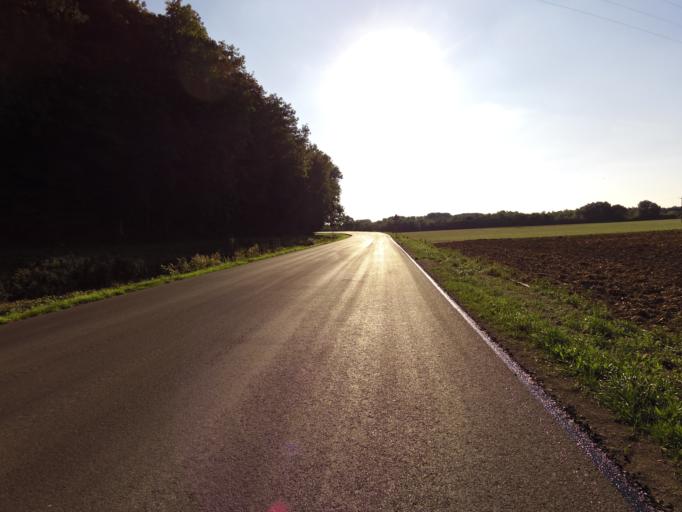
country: DE
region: Bavaria
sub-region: Lower Bavaria
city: Stallwang
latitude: 48.5760
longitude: 12.2367
